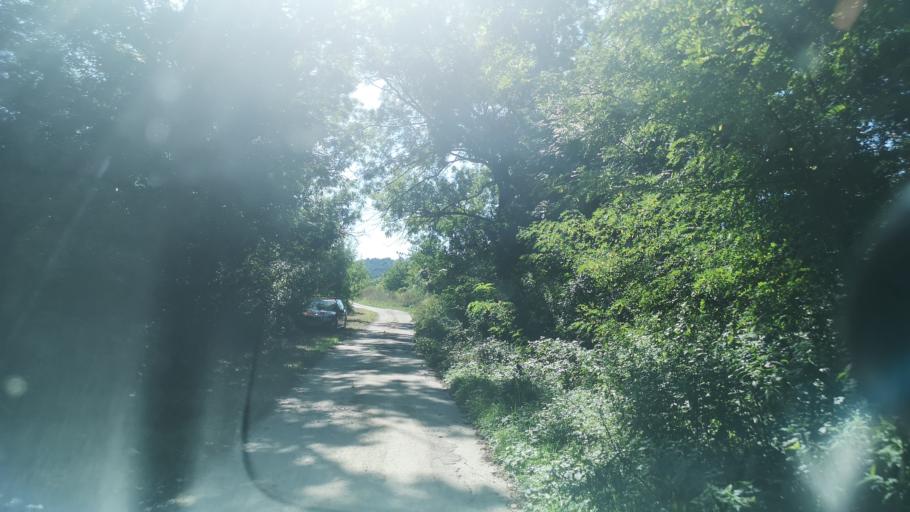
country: SK
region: Trnavsky
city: Smolenice
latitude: 48.5896
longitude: 17.4274
